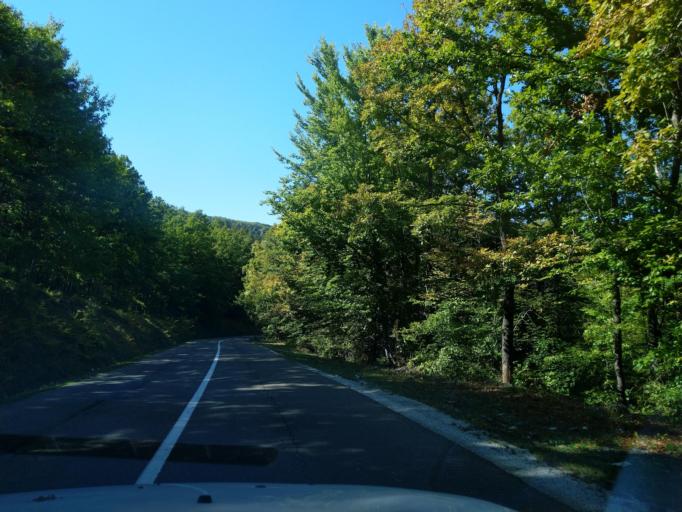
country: RS
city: Sokolovica
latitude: 43.2541
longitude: 20.2509
